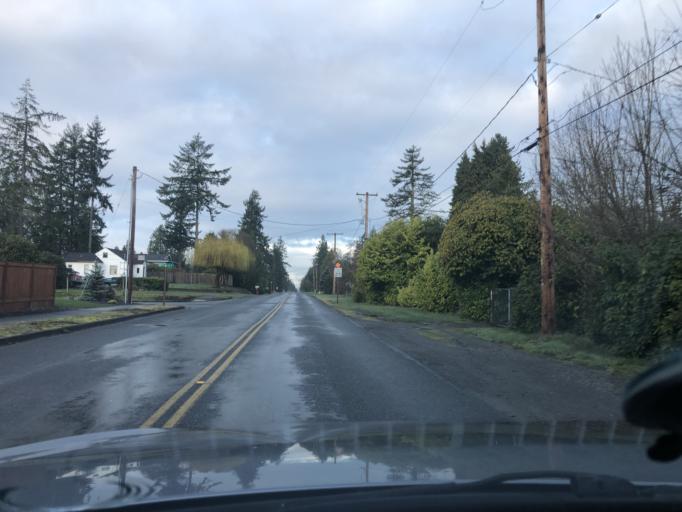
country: US
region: Washington
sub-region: Pierce County
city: Edgewood
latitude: 47.2428
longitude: -122.2959
